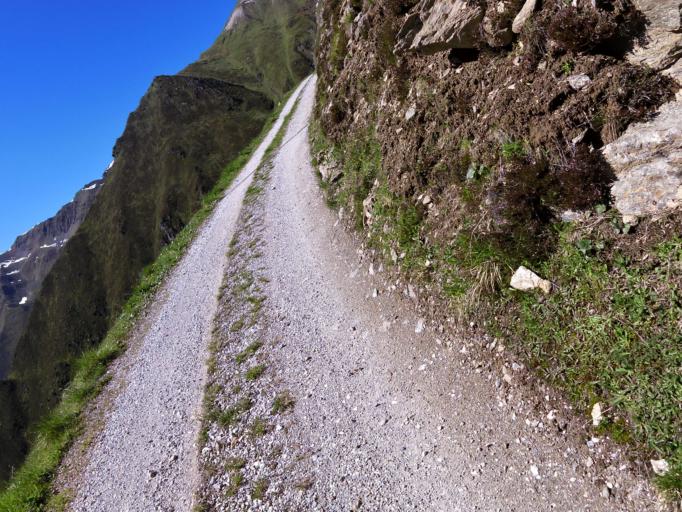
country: AT
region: Tyrol
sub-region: Politischer Bezirk Innsbruck Land
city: Neustift im Stubaital
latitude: 47.1251
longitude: 11.2793
